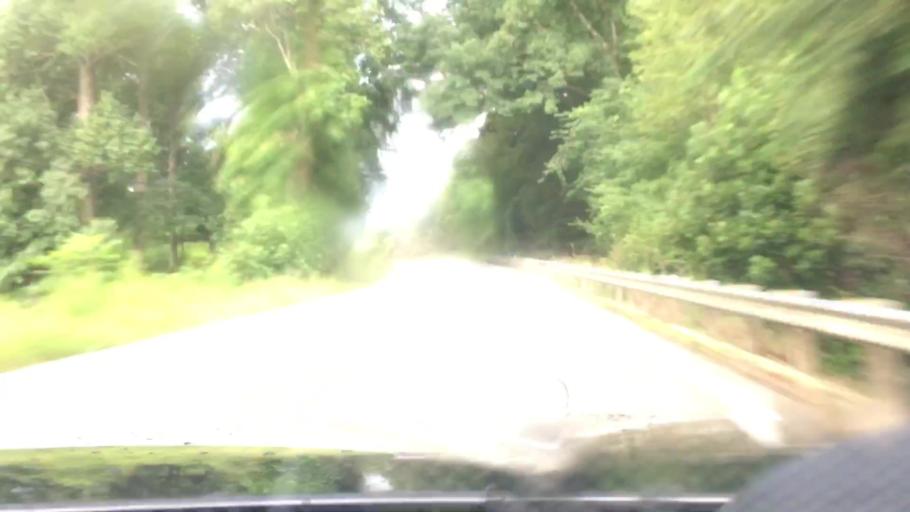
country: US
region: Virginia
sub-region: Nelson County
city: Lovingston
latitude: 37.7761
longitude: -78.9814
